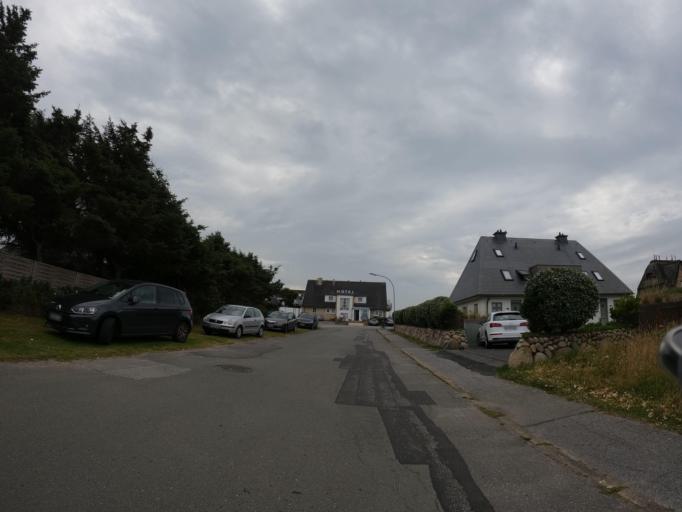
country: DE
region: Schleswig-Holstein
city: Westerland
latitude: 54.9338
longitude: 8.3183
